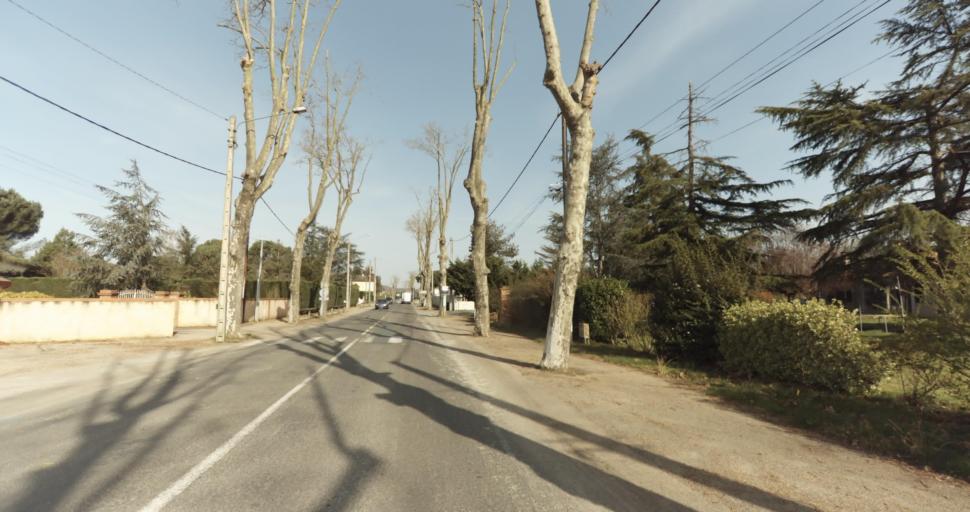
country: FR
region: Midi-Pyrenees
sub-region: Departement du Tarn
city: Saint-Sulpice-la-Pointe
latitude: 43.7638
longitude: 1.6958
